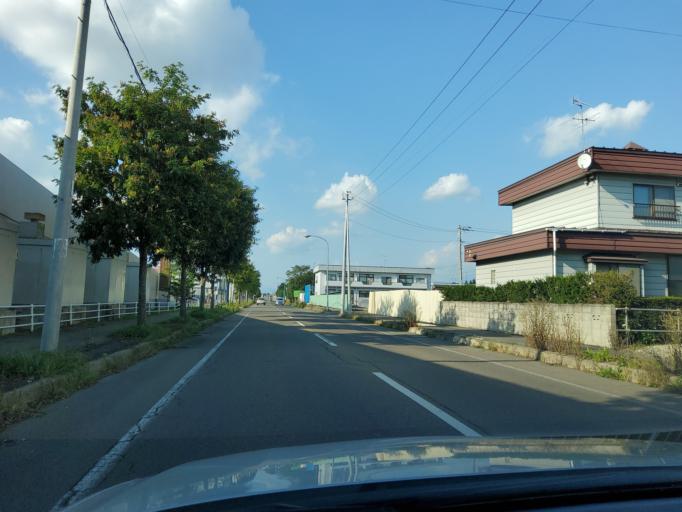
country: JP
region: Hokkaido
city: Obihiro
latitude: 42.8872
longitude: 143.2008
